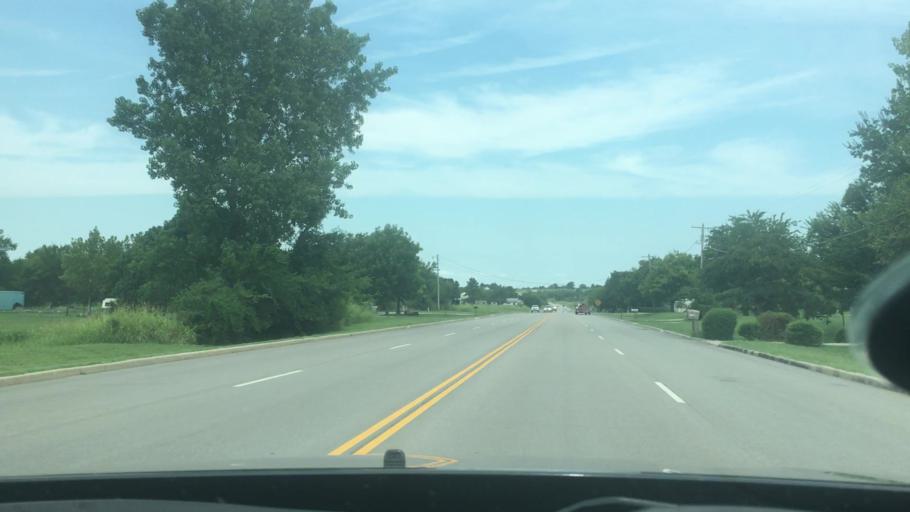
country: US
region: Oklahoma
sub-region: Seminole County
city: Seminole
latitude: 35.2633
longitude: -96.7149
